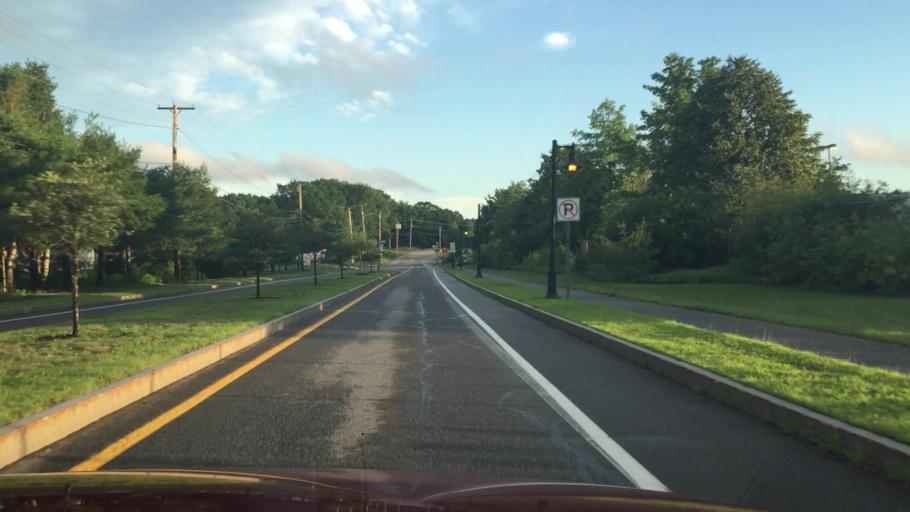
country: US
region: Maine
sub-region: Cumberland County
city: South Portland Gardens
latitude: 43.6707
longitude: -70.3222
